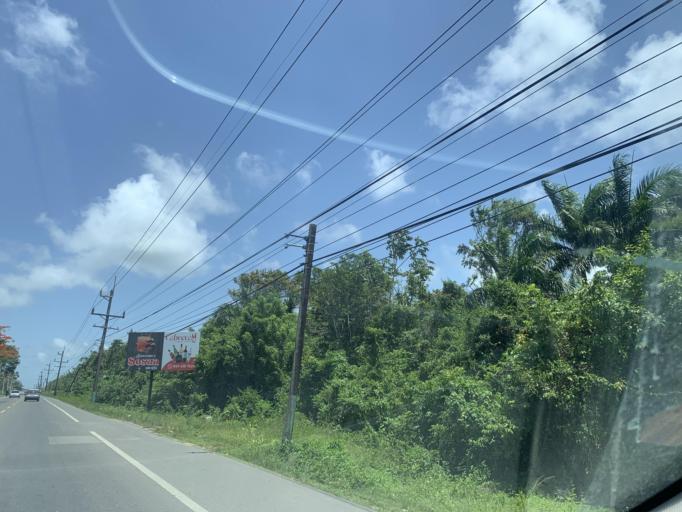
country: DO
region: Puerto Plata
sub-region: Puerto Plata
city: Puerto Plata
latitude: 19.7501
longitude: -70.5687
